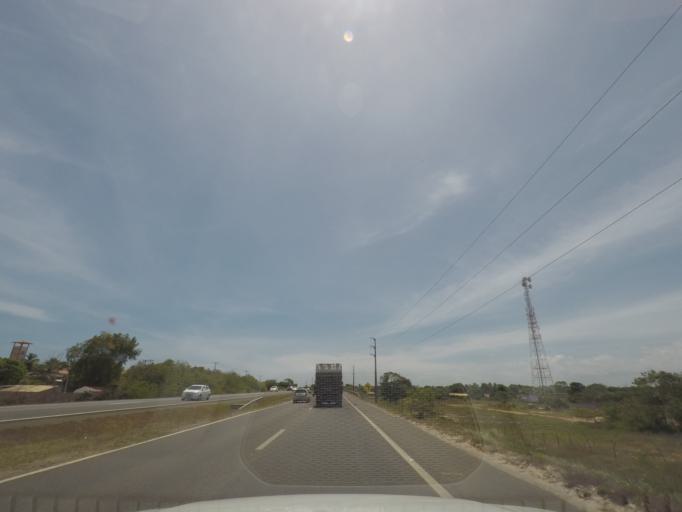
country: BR
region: Bahia
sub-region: Camacari
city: Camacari
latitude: -12.6486
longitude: -38.0810
